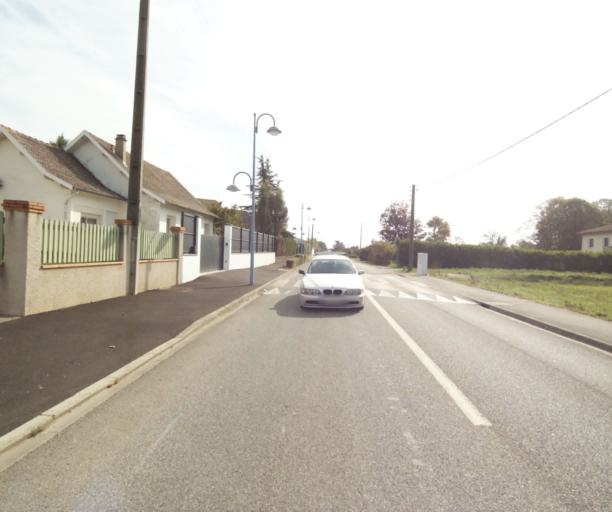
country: FR
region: Midi-Pyrenees
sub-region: Departement du Tarn-et-Garonne
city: Corbarieu
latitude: 43.9425
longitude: 1.3700
